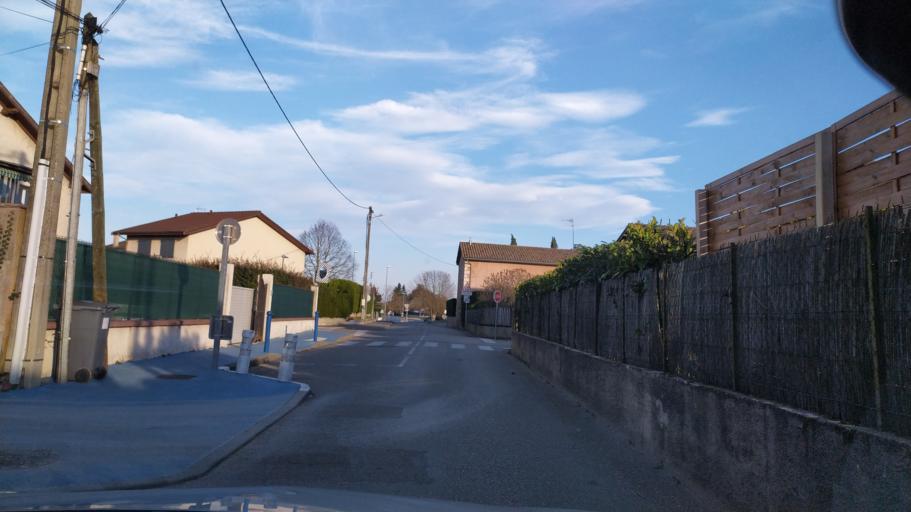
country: FR
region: Rhone-Alpes
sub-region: Departement de l'Isere
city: Charvieu-Chavagneux
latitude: 45.7268
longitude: 5.1486
